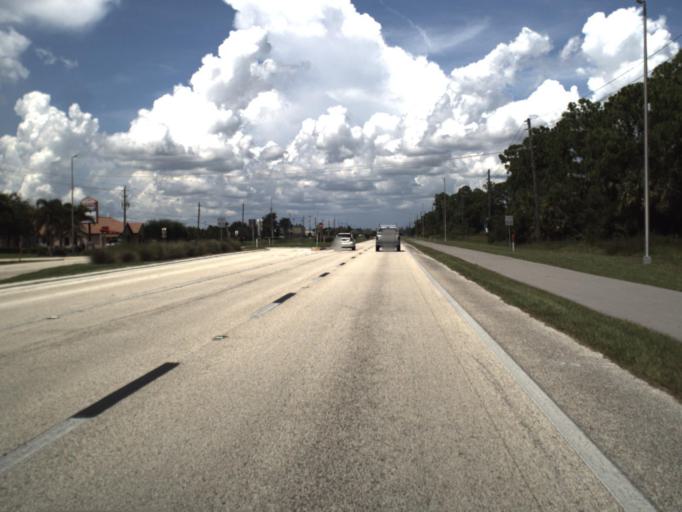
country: US
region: Florida
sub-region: Charlotte County
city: Charlotte Park
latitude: 26.8923
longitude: -82.0243
